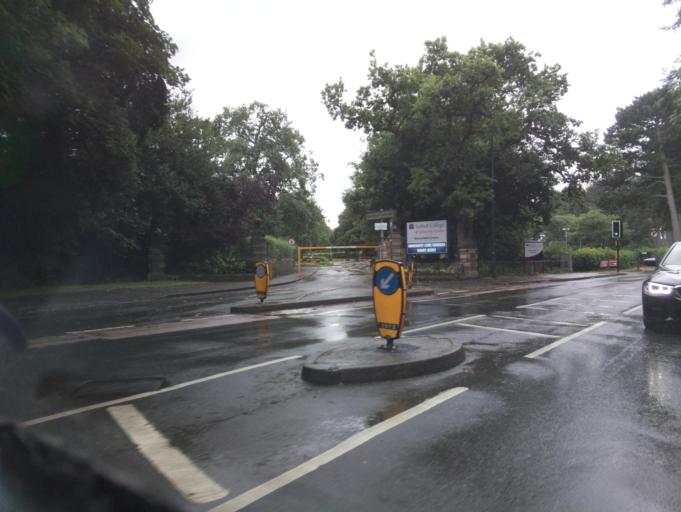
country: GB
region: England
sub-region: Solihull
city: Solihull
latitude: 52.4103
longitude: -1.7934
